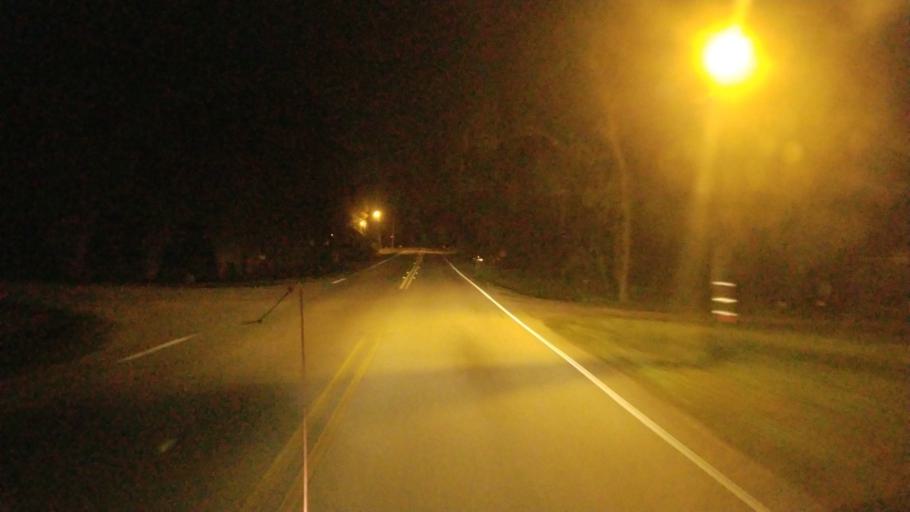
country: US
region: Florida
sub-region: Marion County
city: Ocala
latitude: 29.1687
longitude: -82.2517
